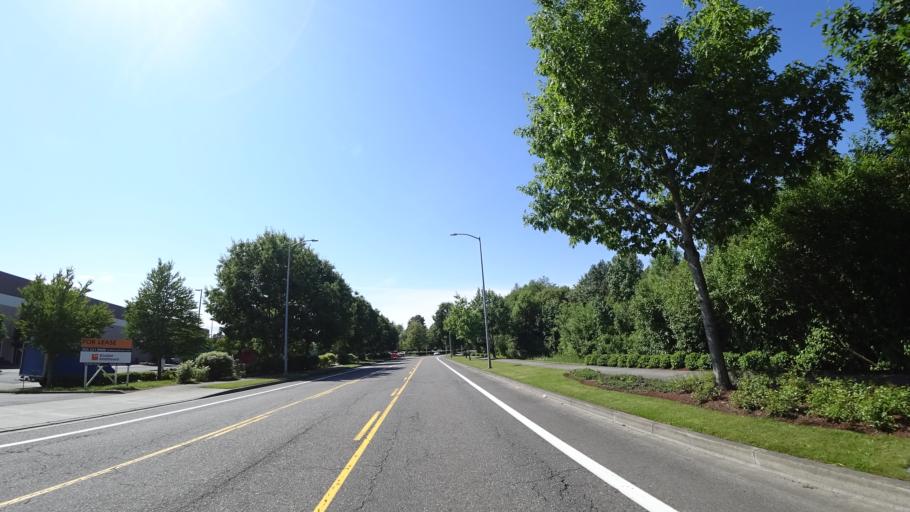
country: US
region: Oregon
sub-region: Multnomah County
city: Lents
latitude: 45.5713
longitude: -122.5720
